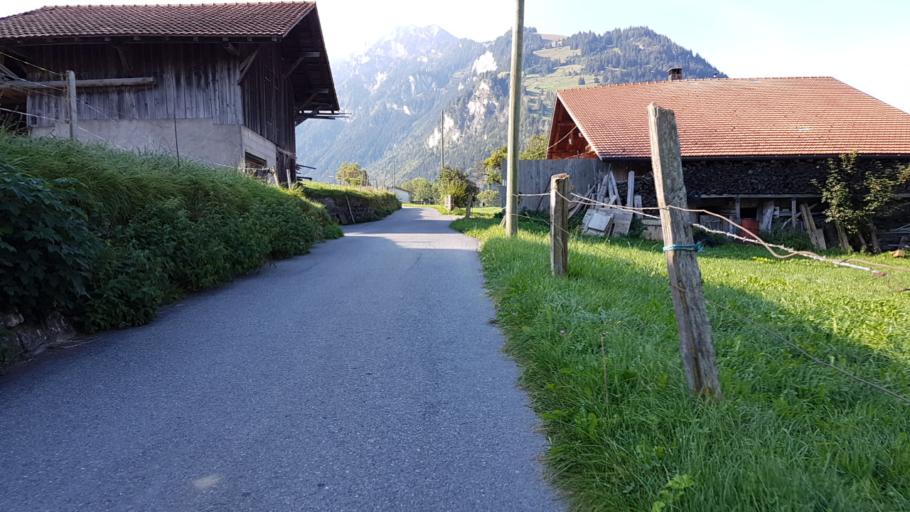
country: CH
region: Bern
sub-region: Frutigen-Niedersimmental District
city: Frutigen
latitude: 46.5786
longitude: 7.6577
